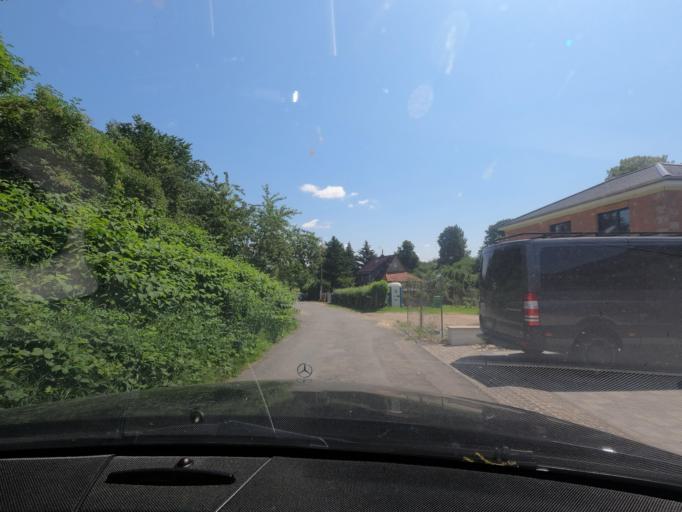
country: DE
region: Thuringia
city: Muehlhausen
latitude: 51.2089
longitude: 10.4287
